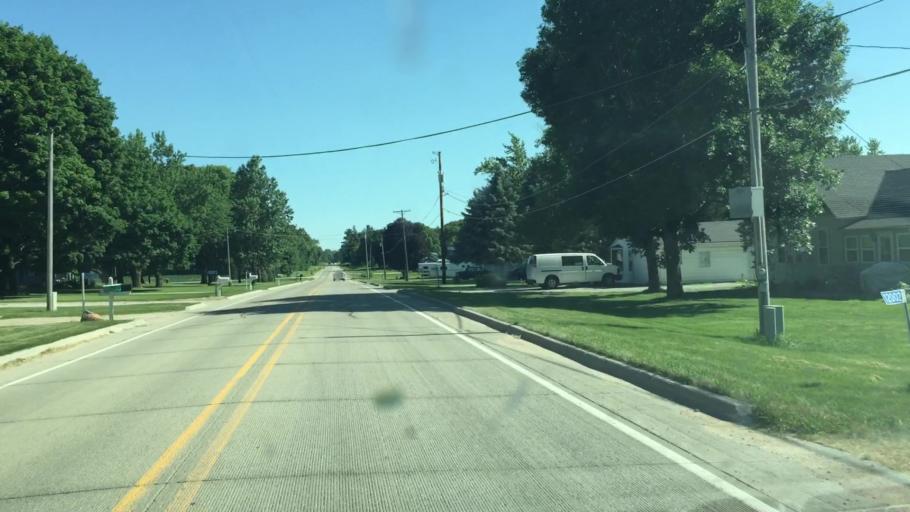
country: US
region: Iowa
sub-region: Linn County
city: Ely
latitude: 41.8646
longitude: -91.6464
